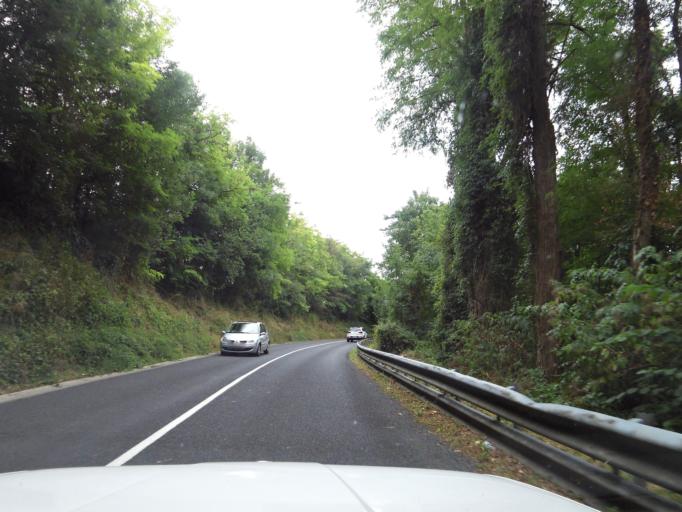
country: FR
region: Rhone-Alpes
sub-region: Departement de l'Ain
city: Chazey-sur-Ain
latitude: 45.8986
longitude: 5.2517
